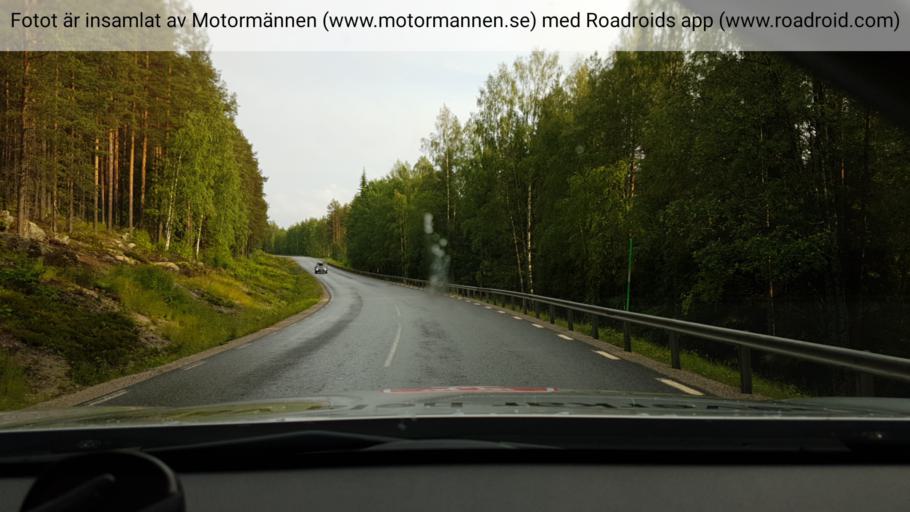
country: SE
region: Vaesterbotten
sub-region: Lycksele Kommun
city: Lycksele
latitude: 64.4202
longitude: 19.0041
